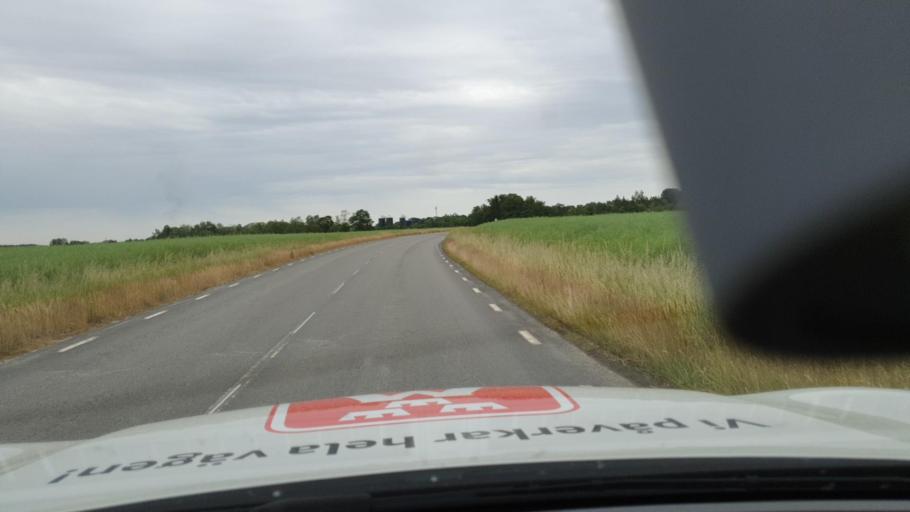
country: SE
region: Vaestra Goetaland
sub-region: Tidaholms Kommun
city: Olofstorp
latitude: 58.3024
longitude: 14.0829
